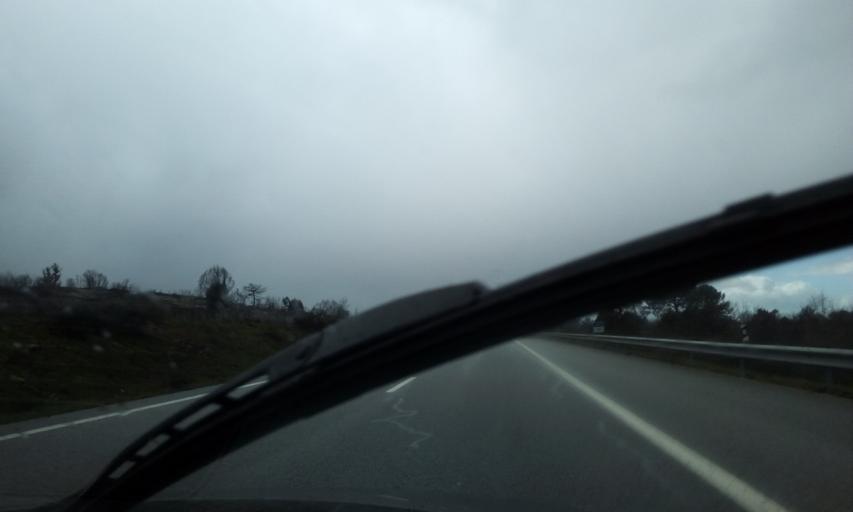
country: PT
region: Viseu
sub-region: Mangualde
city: Mangualde
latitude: 40.6136
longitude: -7.6971
